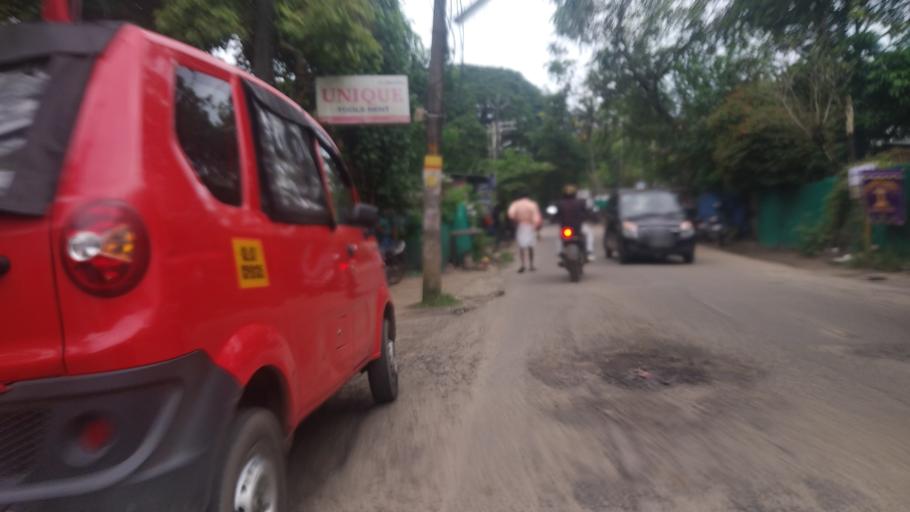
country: IN
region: Kerala
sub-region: Alappuzha
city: Arukutti
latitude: 9.8699
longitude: 76.2907
